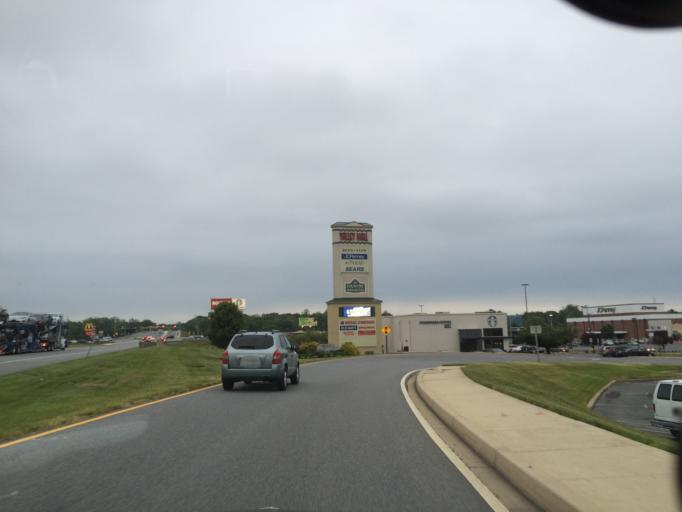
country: US
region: Maryland
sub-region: Washington County
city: Halfway
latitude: 39.6273
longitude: -77.7705
